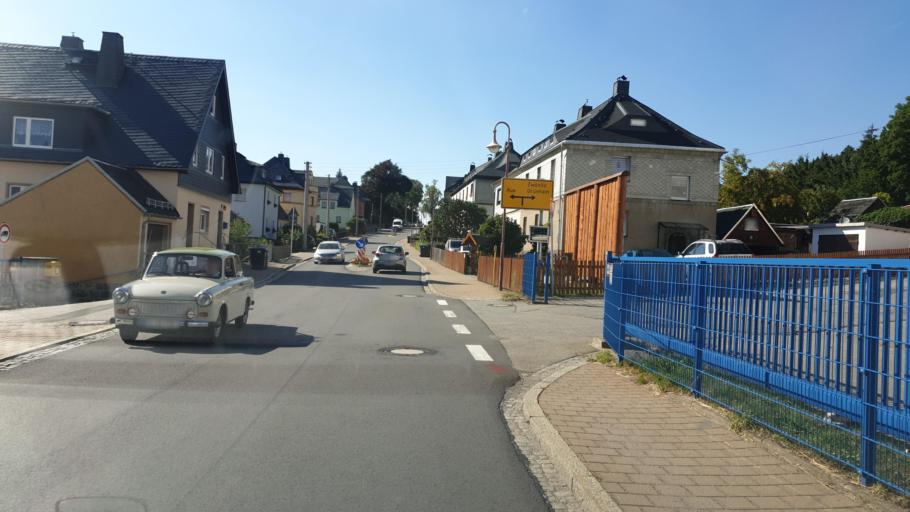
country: DE
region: Saxony
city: Bernsbach
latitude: 50.5814
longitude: 12.7647
